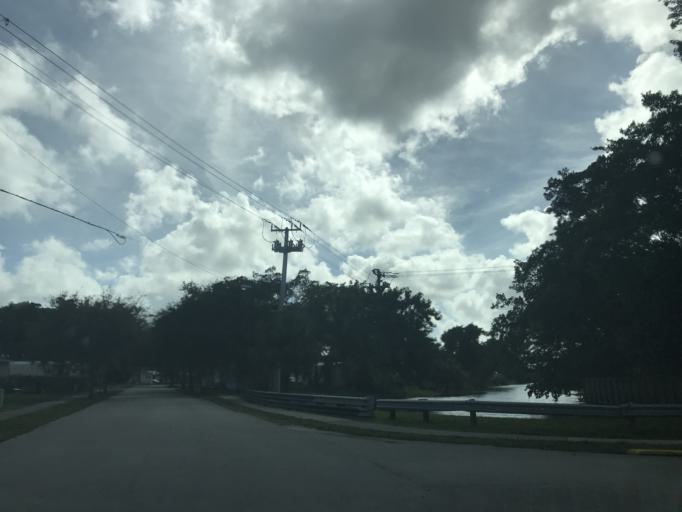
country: US
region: Florida
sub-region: Palm Beach County
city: Boca Pointe
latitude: 26.3126
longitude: -80.1771
